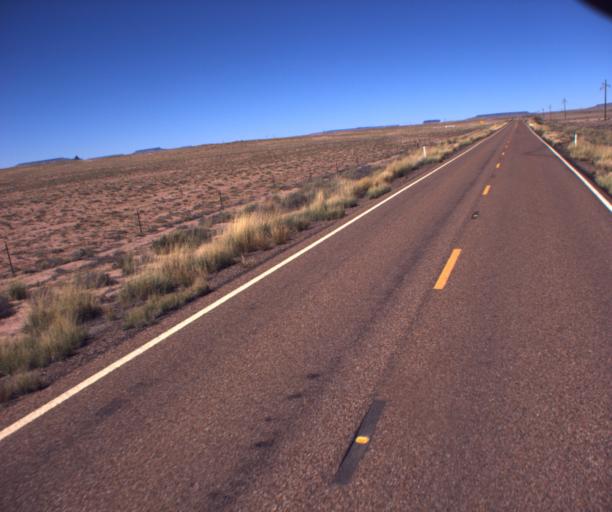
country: US
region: Arizona
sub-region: Navajo County
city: Holbrook
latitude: 35.1014
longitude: -110.0956
